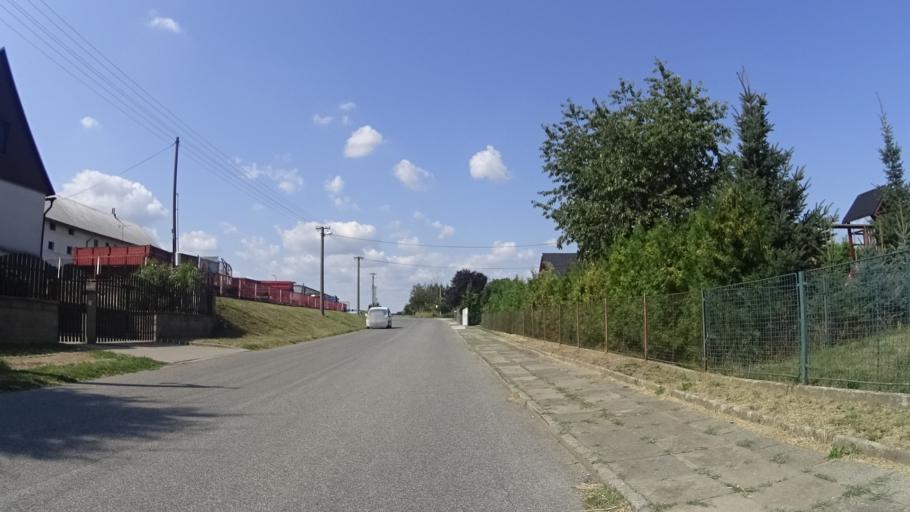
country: CZ
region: Kralovehradecky
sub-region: Okres Jicin
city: Jicin
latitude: 50.3682
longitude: 15.3761
